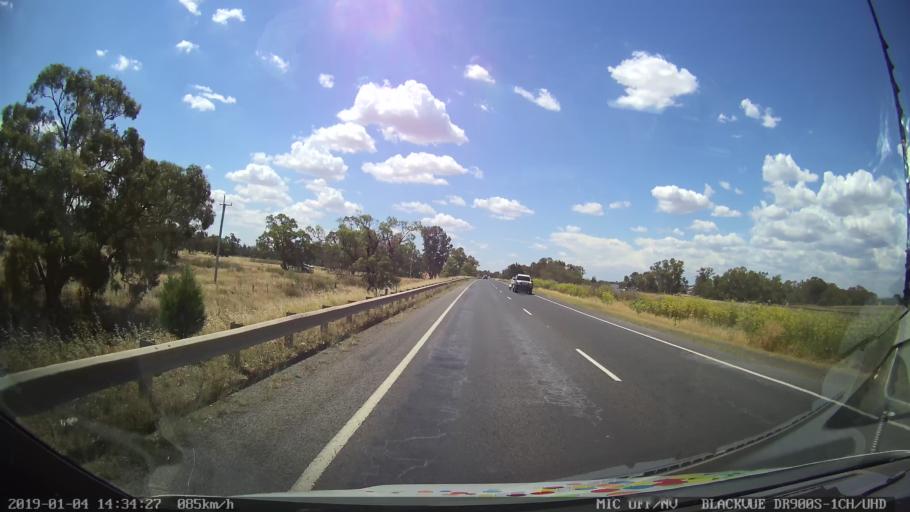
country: AU
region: New South Wales
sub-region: Dubbo Municipality
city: Dubbo
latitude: -32.1983
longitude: 148.6204
